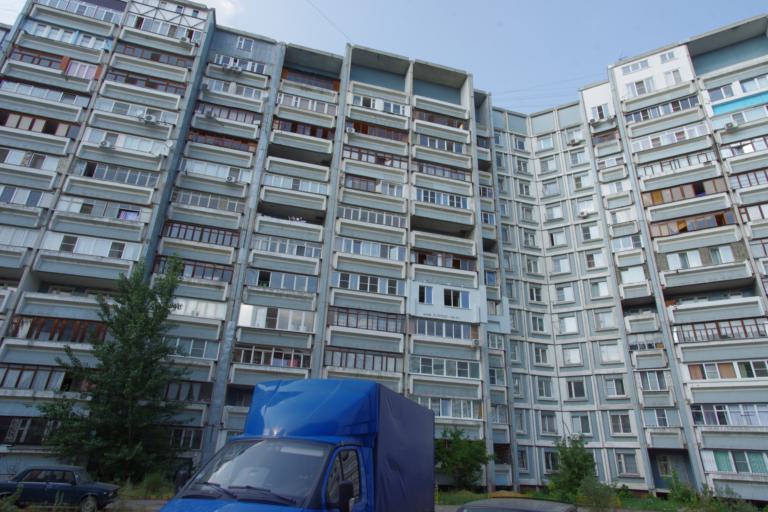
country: RU
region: Nizjnij Novgorod
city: Nizhniy Novgorod
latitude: 56.3438
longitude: 43.9433
